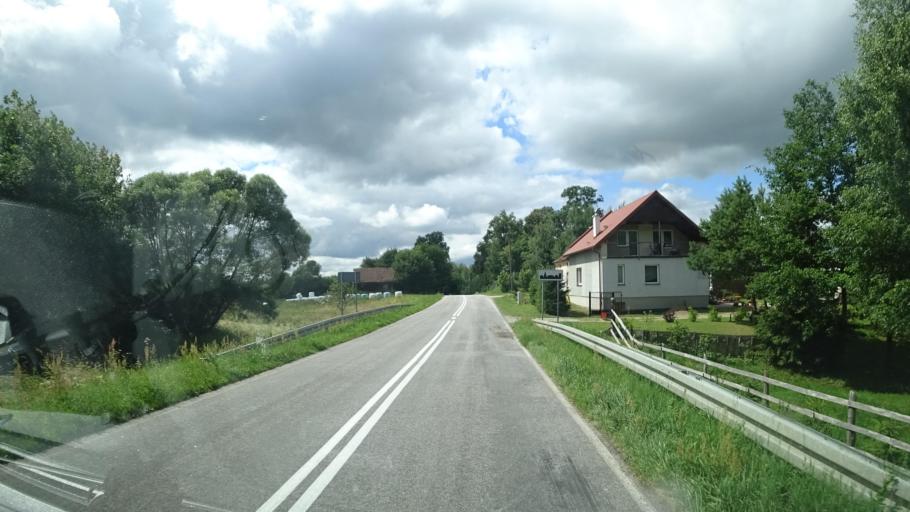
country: PL
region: Warmian-Masurian Voivodeship
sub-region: Powiat goldapski
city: Goldap
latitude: 54.2079
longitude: 22.1973
